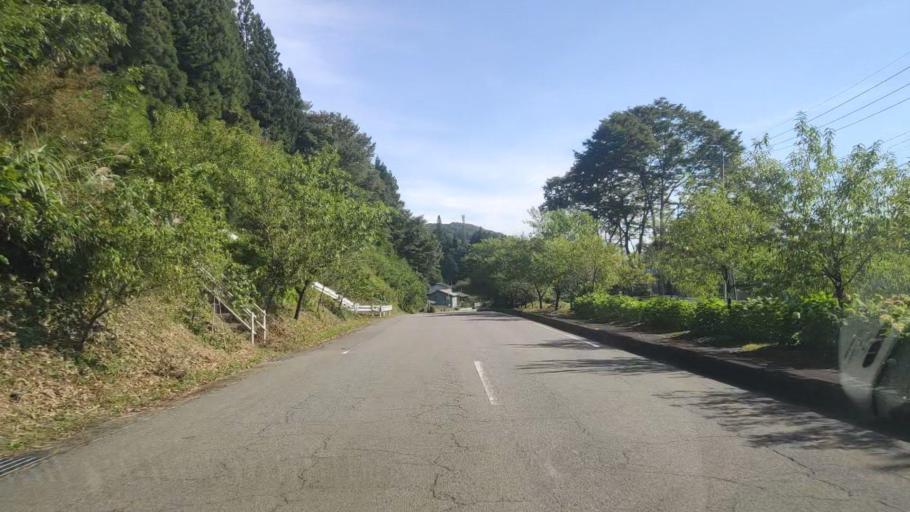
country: JP
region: Gunma
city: Nakanojomachi
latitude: 36.6065
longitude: 138.7206
